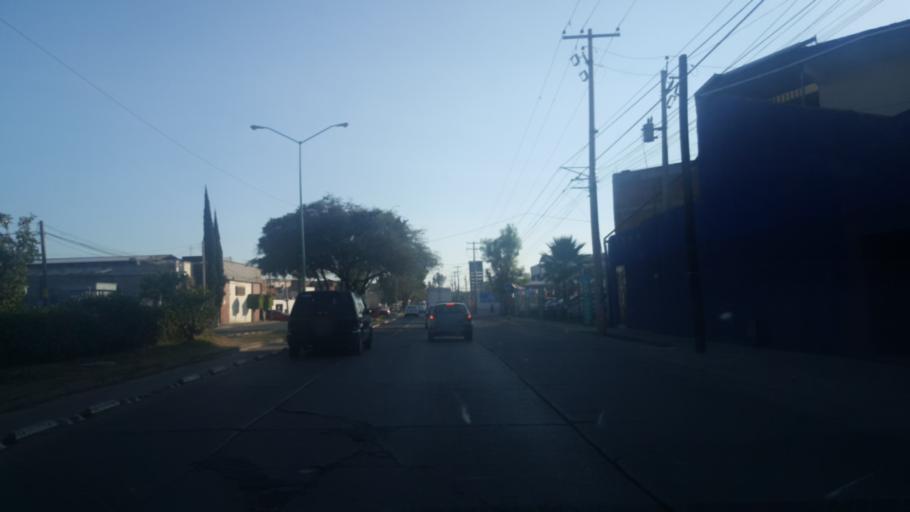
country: MX
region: Guanajuato
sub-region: Leon
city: Medina
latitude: 21.1138
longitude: -101.6347
